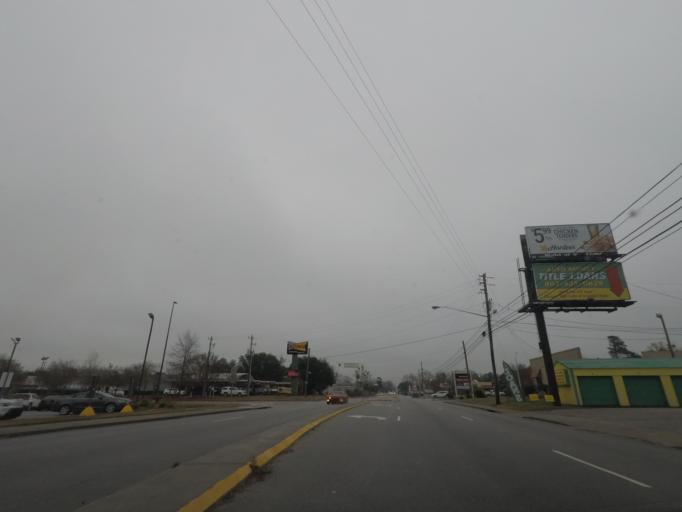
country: US
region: South Carolina
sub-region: Clarendon County
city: Manning
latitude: 33.6975
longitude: -80.2262
